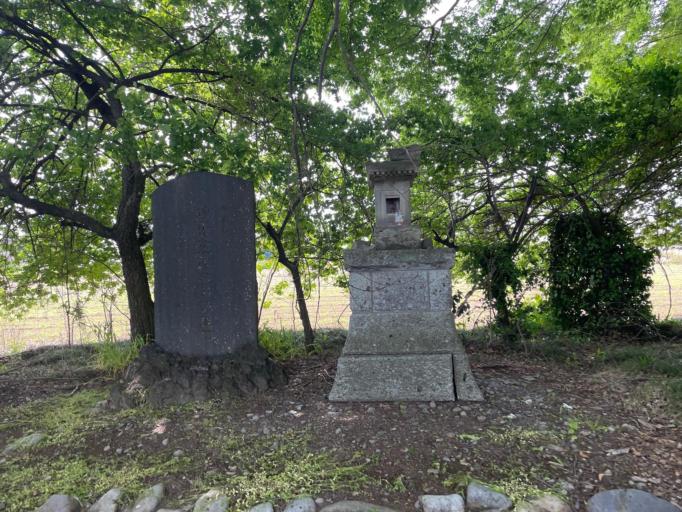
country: JP
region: Tochigi
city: Mibu
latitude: 36.4532
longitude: 139.7745
